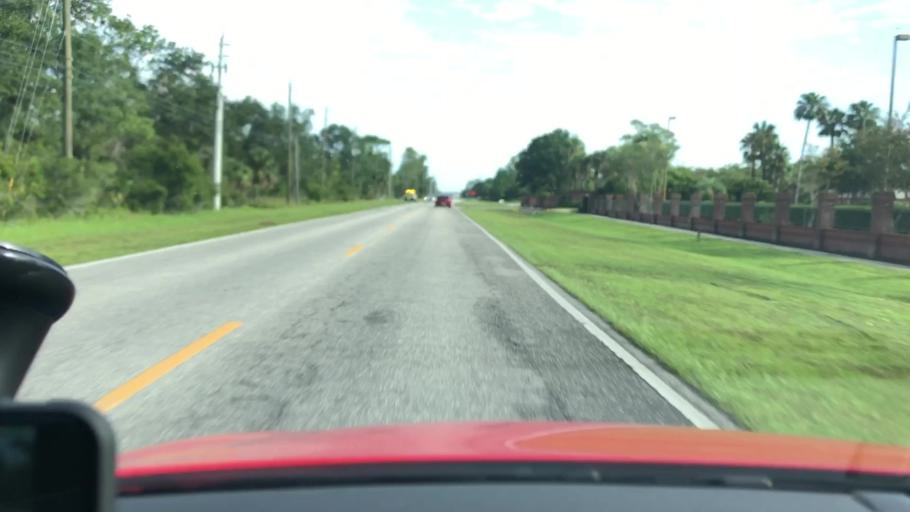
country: US
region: Florida
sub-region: Volusia County
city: Daytona Beach
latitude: 29.1747
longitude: -81.0898
